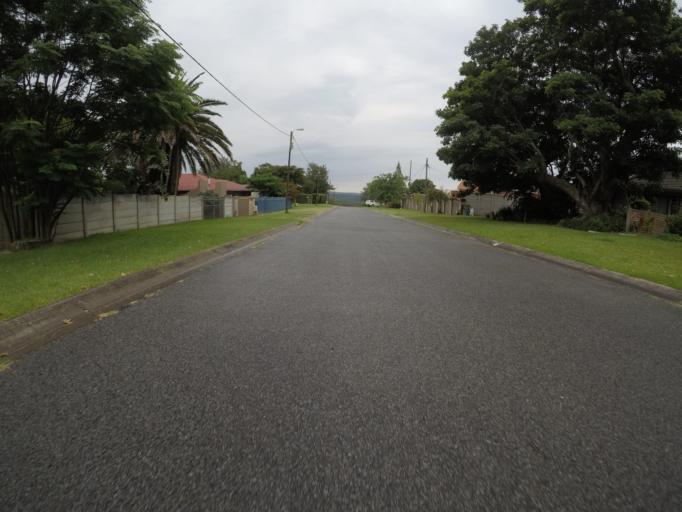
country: ZA
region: Eastern Cape
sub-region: Buffalo City Metropolitan Municipality
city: East London
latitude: -32.9661
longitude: 27.8482
